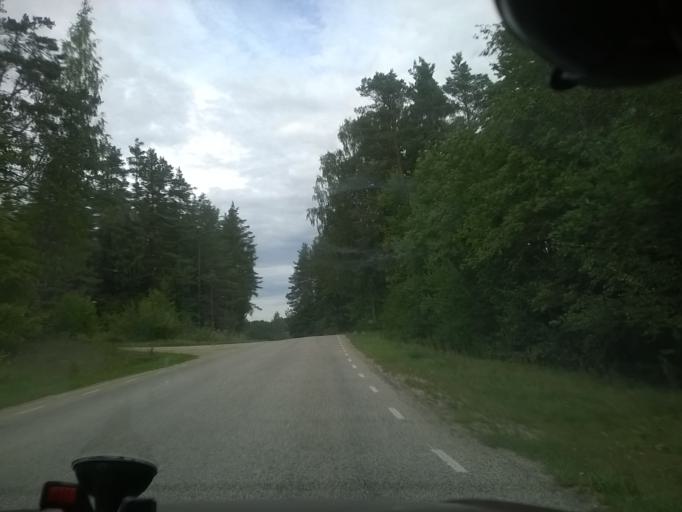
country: EE
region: Vorumaa
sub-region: Voru linn
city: Voru
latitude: 57.7746
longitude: 27.0256
